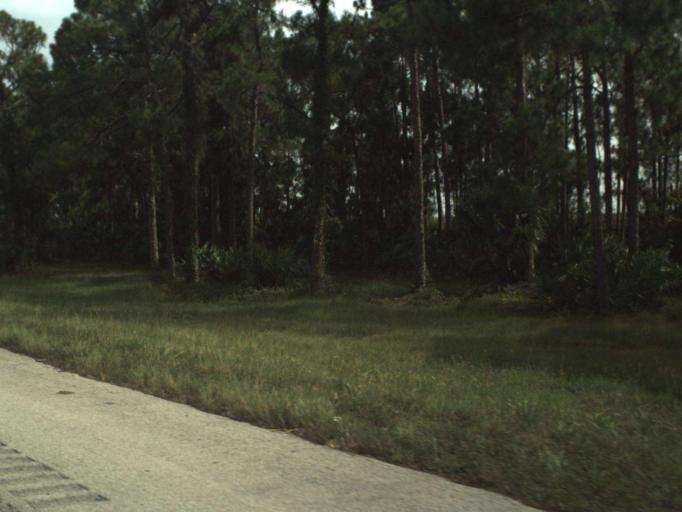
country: US
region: Florida
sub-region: Saint Lucie County
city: Port Saint Lucie
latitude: 27.2266
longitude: -80.4032
